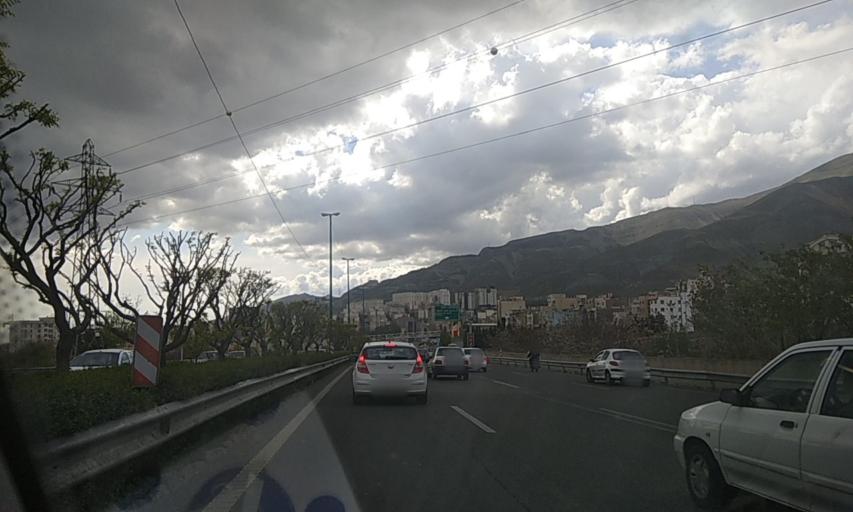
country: IR
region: Tehran
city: Tajrish
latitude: 35.7840
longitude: 51.3550
